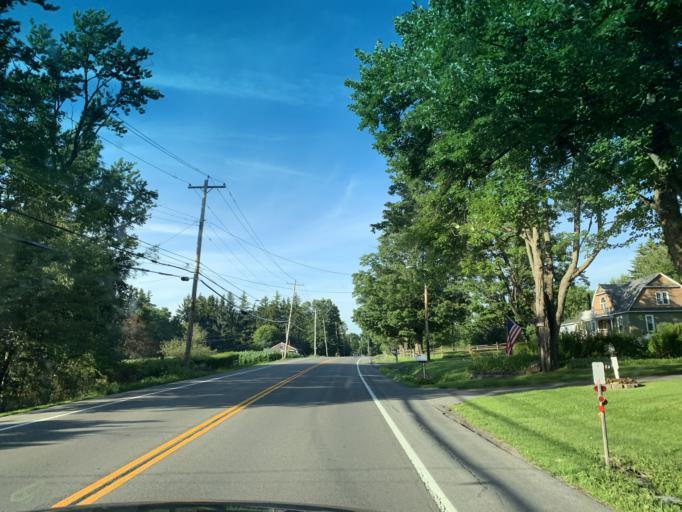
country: US
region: New York
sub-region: Oneida County
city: Clinton
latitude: 43.0612
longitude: -75.3590
